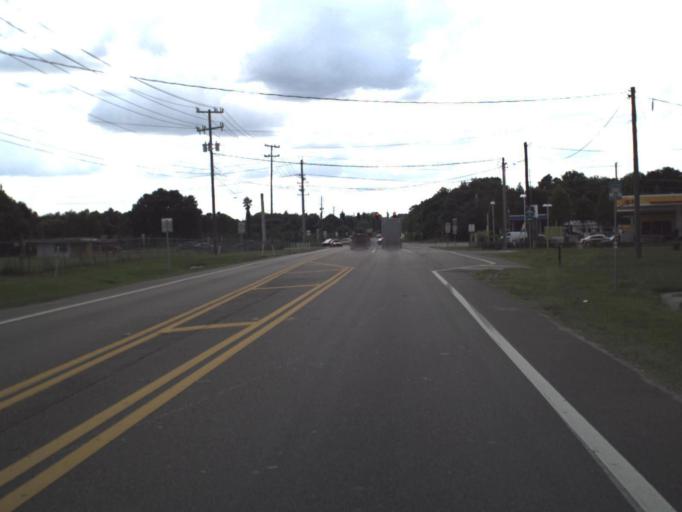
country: US
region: Florida
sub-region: Polk County
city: Winston
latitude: 28.0356
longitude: -82.0174
